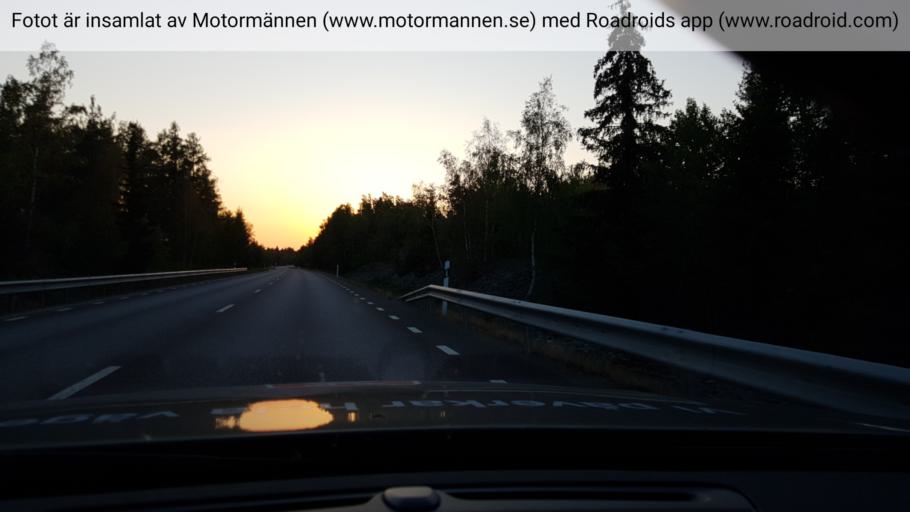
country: SE
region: Uppsala
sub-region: Osthammars Kommun
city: Bjorklinge
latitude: 59.9761
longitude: 17.3529
